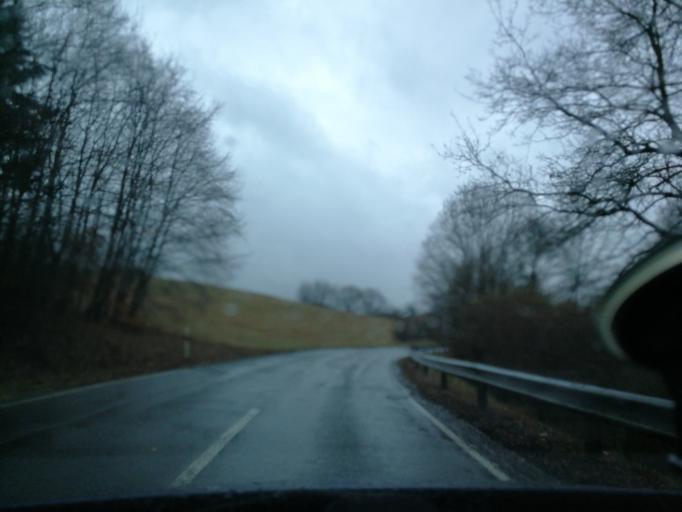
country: DE
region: Rheinland-Pfalz
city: Berglicht
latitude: 49.7933
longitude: 6.9648
